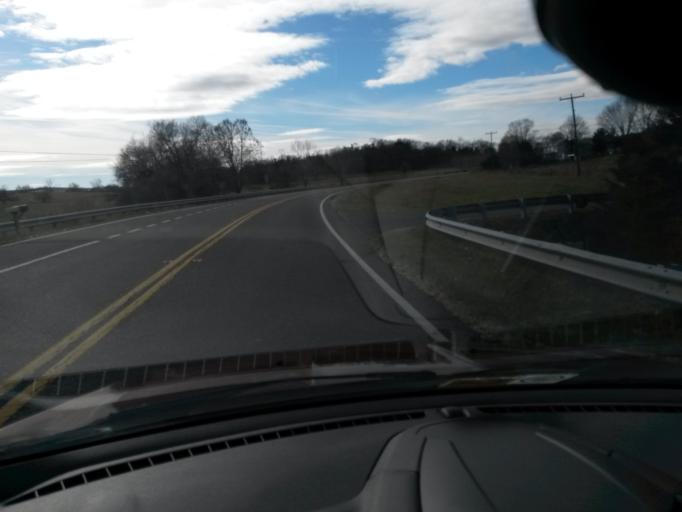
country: US
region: Virginia
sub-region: Rockingham County
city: Bridgewater
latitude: 38.3726
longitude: -78.9906
